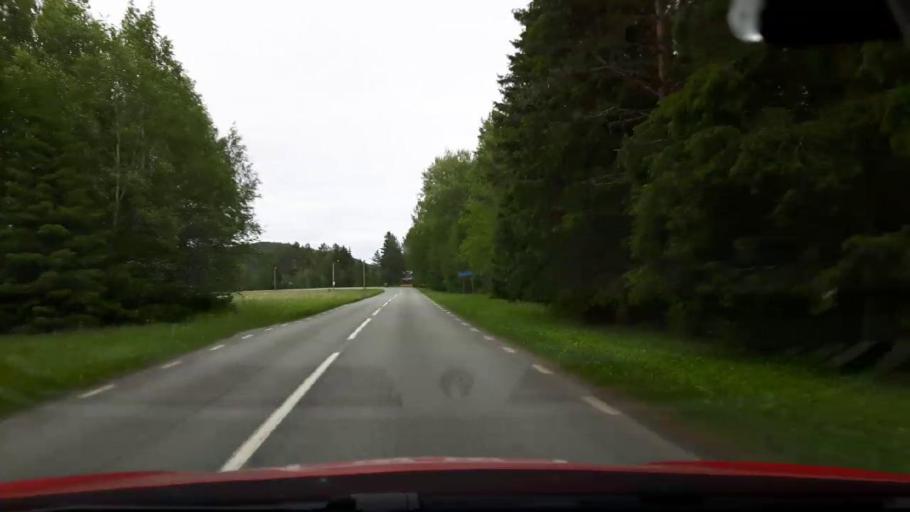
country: SE
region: Jaemtland
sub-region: Stroemsunds Kommun
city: Stroemsund
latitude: 63.4149
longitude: 15.5778
